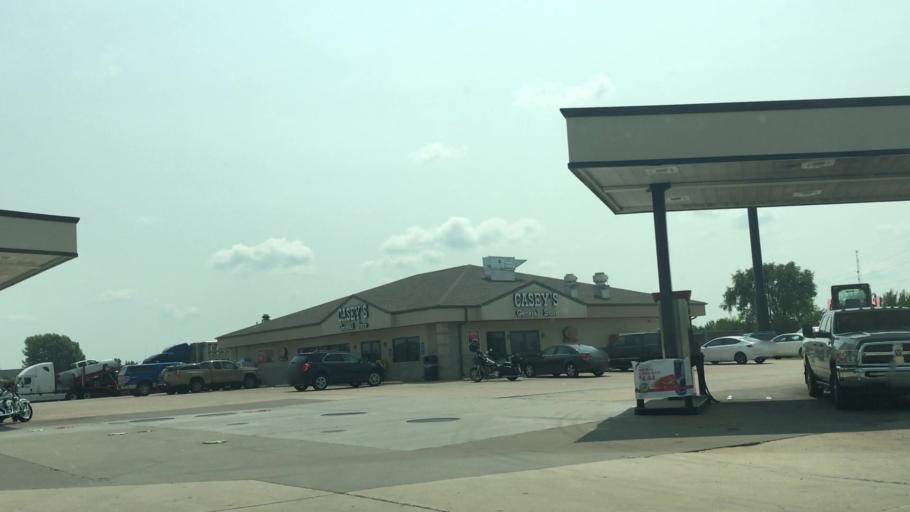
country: US
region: Iowa
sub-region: Benton County
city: Urbana
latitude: 42.2471
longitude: -91.8898
